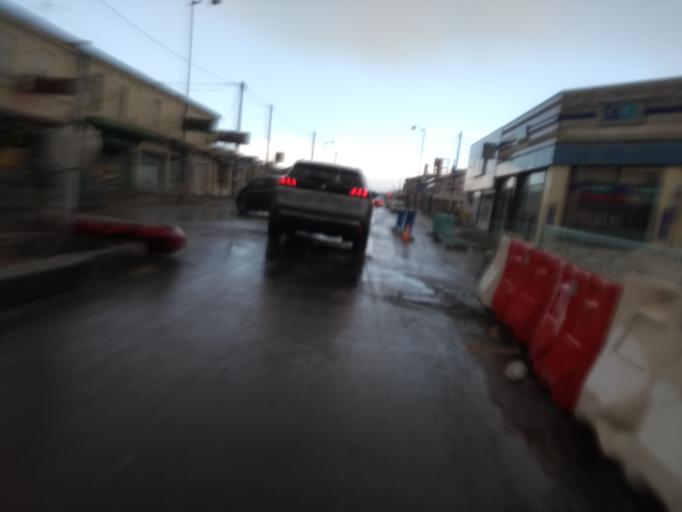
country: FR
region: Aquitaine
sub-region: Departement de la Gironde
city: Villenave-d'Ornon
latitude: 44.7832
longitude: -0.5660
